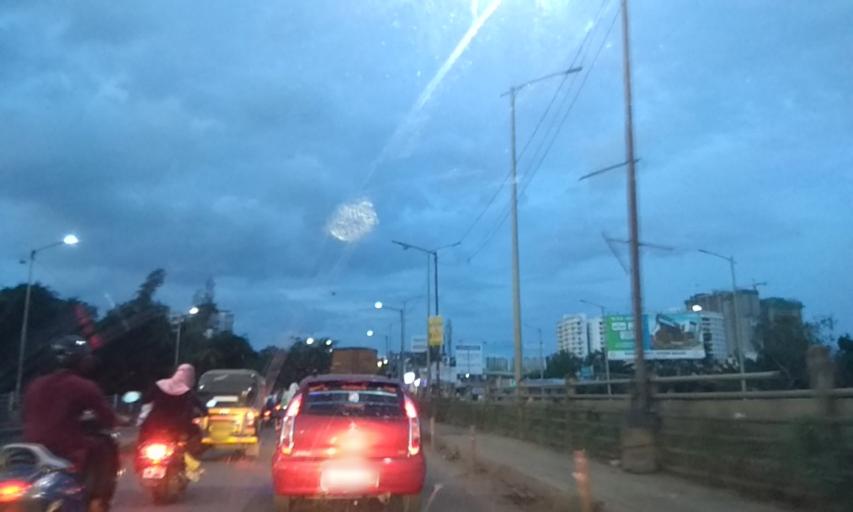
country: IN
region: Maharashtra
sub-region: Pune Division
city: Lohogaon
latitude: 18.5365
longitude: 73.9339
